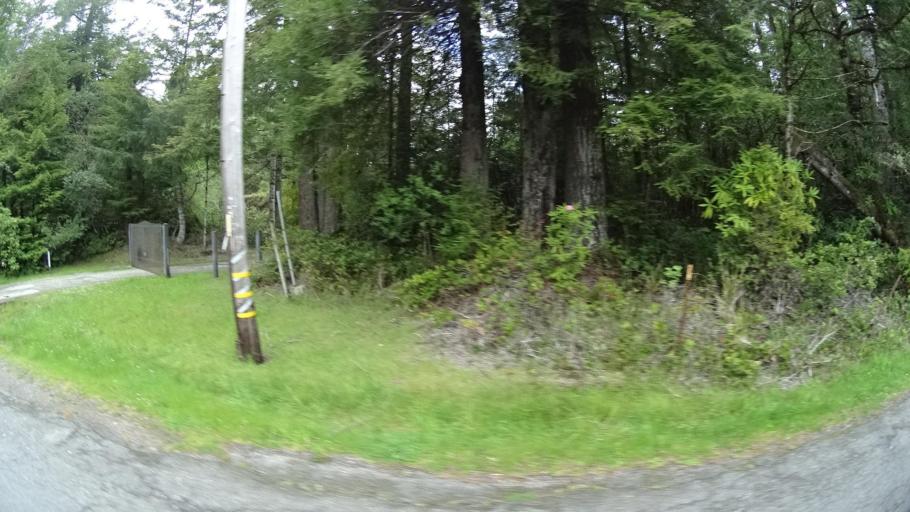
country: US
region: California
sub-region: Humboldt County
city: Blue Lake
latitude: 40.8192
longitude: -123.9963
